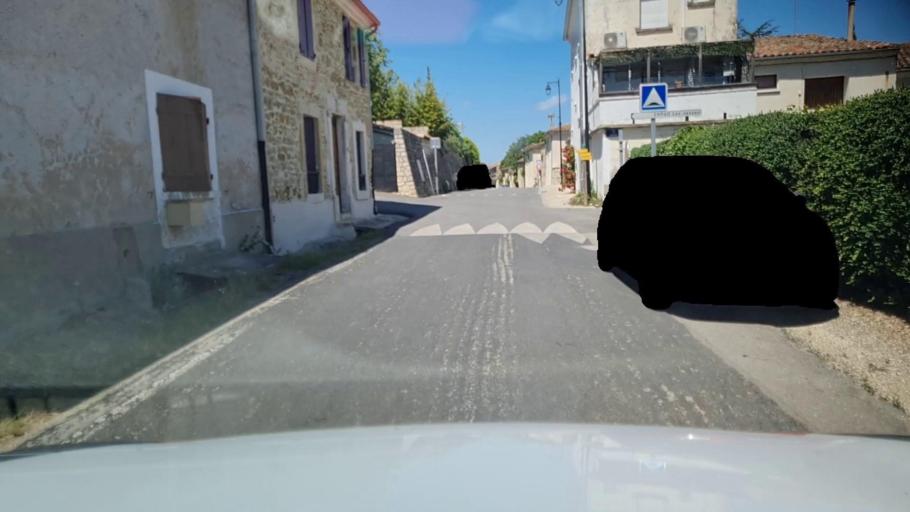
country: FR
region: Languedoc-Roussillon
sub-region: Departement du Gard
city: Saint-Mamert-du-Gard
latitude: 43.9056
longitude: 4.1933
